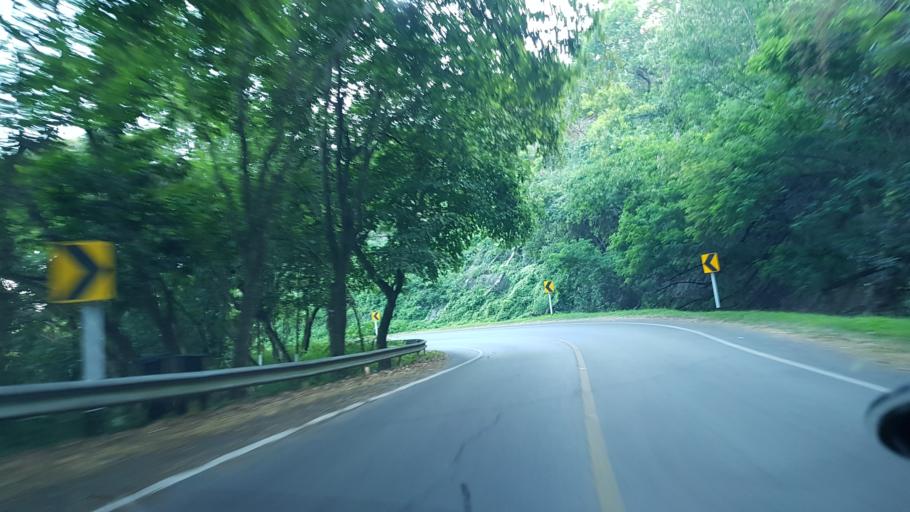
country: TH
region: Chiang Rai
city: Mae Fa Luang
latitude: 20.2953
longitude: 99.8154
